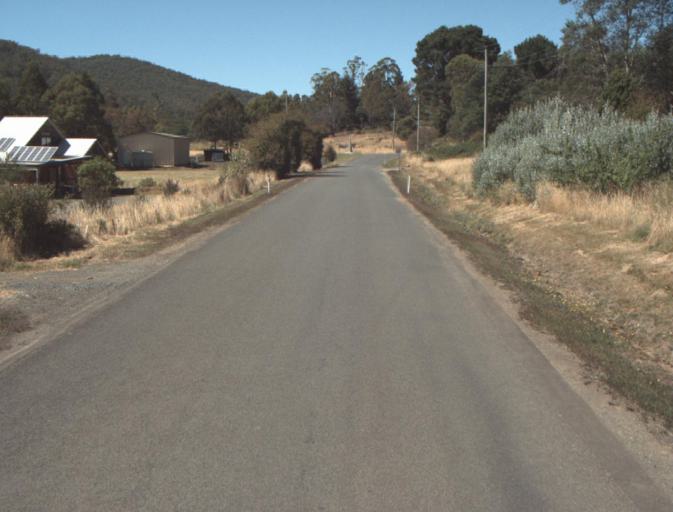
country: AU
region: Tasmania
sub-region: Launceston
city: Newstead
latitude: -41.3891
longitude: 147.2967
